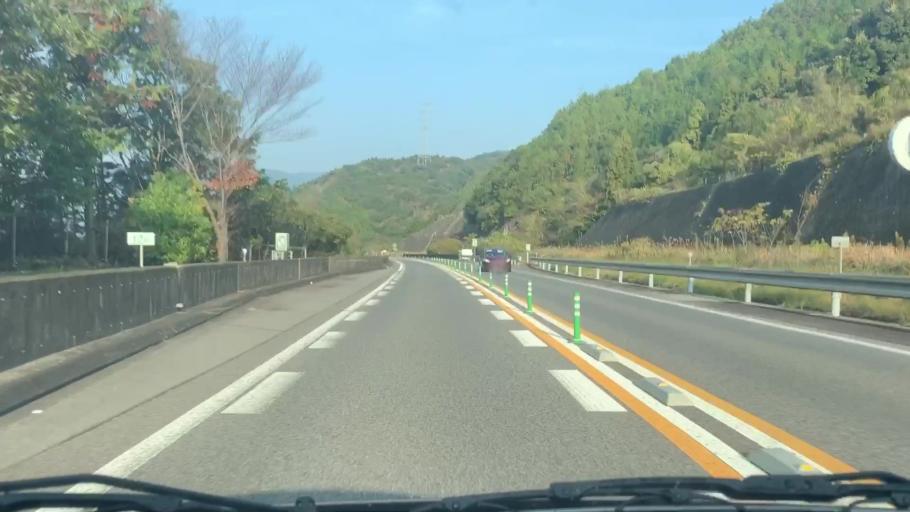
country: JP
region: Saga Prefecture
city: Imaricho-ko
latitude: 33.1632
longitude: 129.8635
